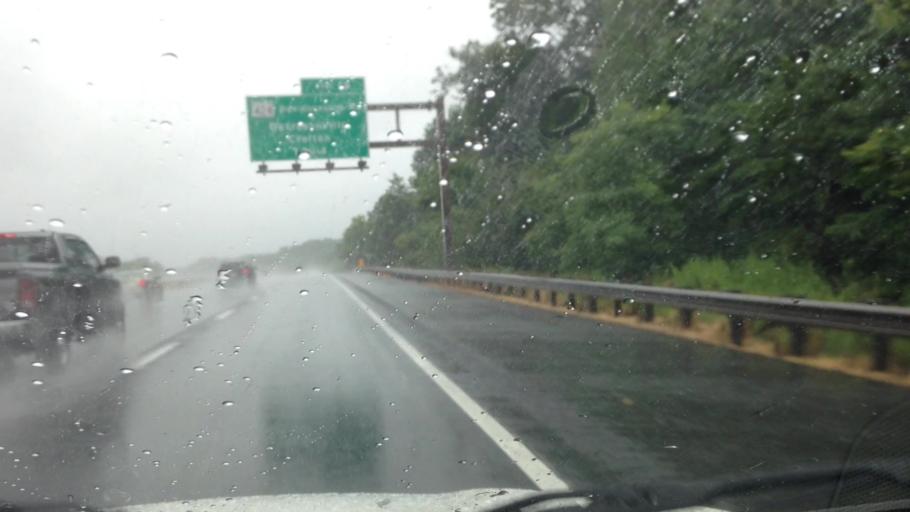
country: US
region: Maryland
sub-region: Anne Arundel County
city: Crofton
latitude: 38.9558
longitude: -76.6812
